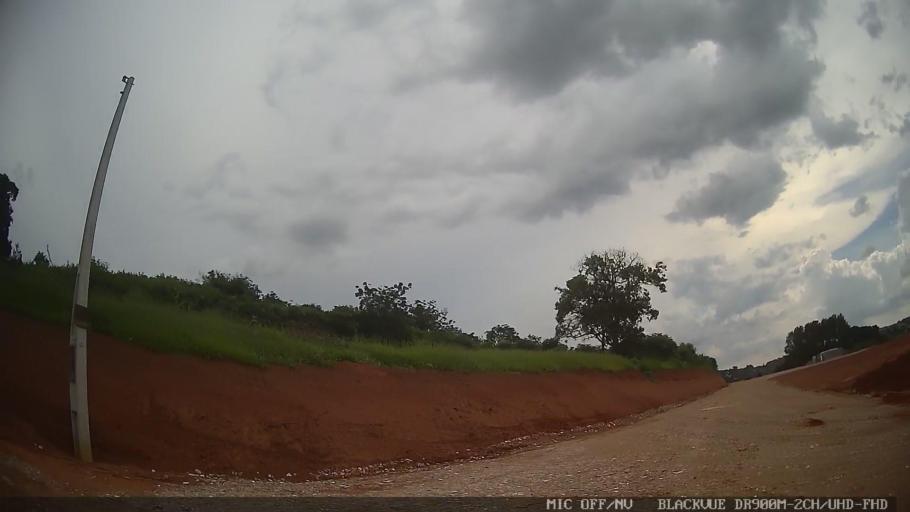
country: BR
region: Sao Paulo
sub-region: Atibaia
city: Atibaia
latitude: -23.1478
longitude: -46.5709
